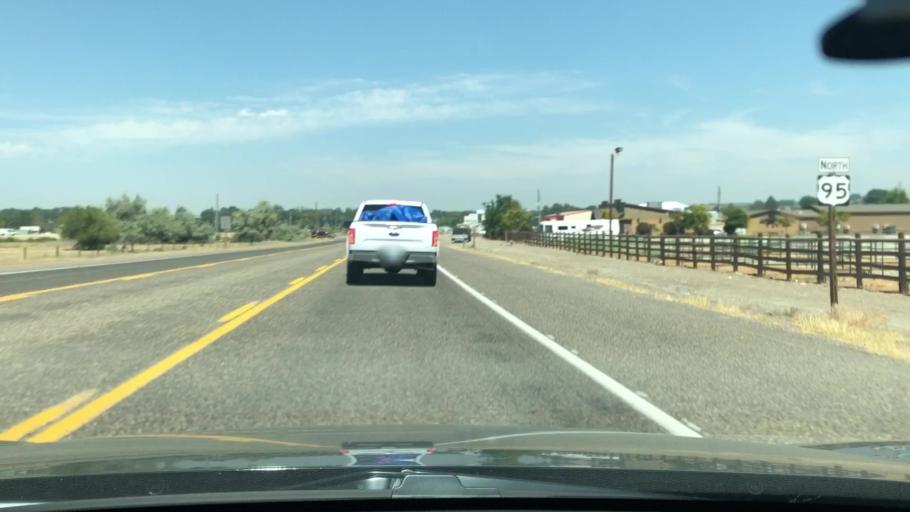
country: US
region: Idaho
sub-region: Owyhee County
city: Homedale
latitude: 43.6125
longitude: -116.9289
